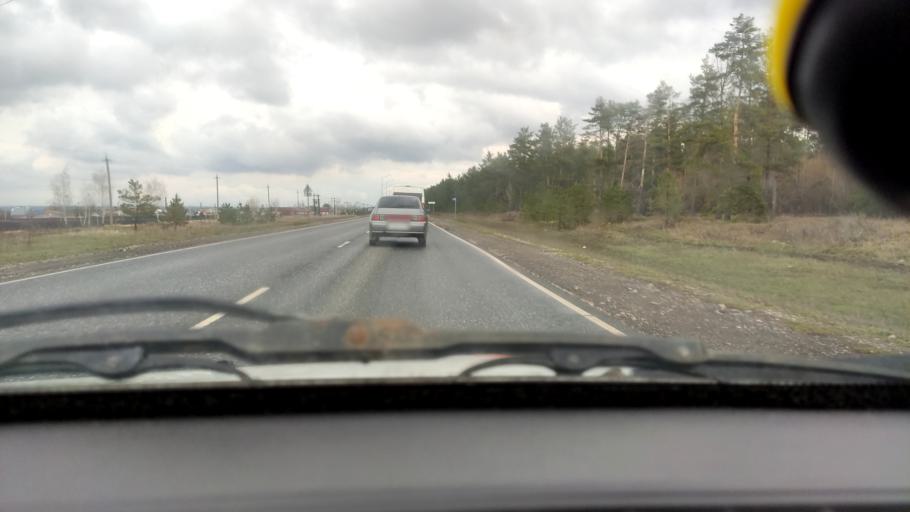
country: RU
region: Samara
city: Zhigulevsk
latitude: 53.5770
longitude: 49.5596
